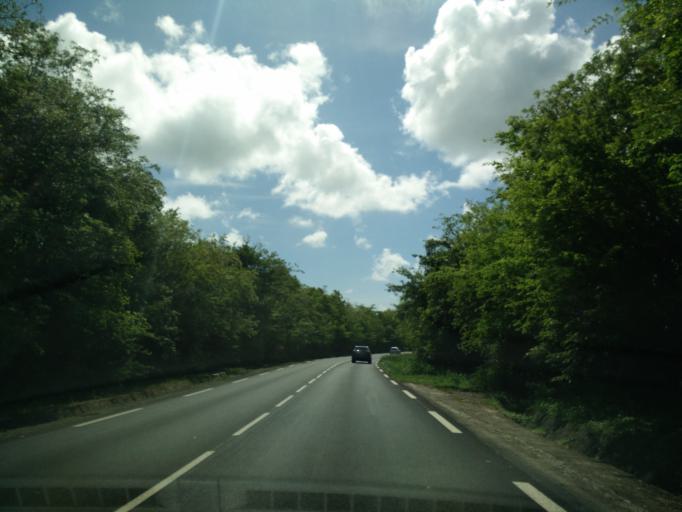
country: MQ
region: Martinique
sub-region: Martinique
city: Les Trois-Ilets
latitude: 14.5291
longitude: -61.0193
